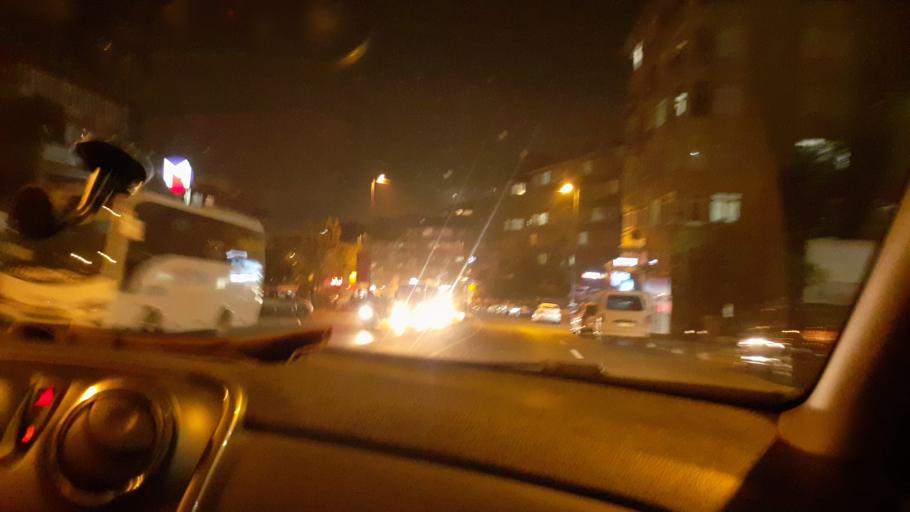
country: TR
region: Istanbul
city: UEskuedar
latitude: 41.0281
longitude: 29.0286
